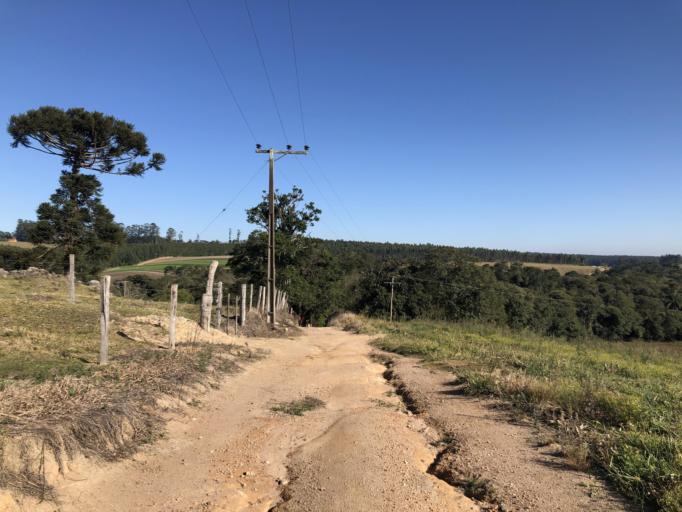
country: BR
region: Sao Paulo
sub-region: Pilar Do Sul
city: Pilar do Sul
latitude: -23.8295
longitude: -47.6248
